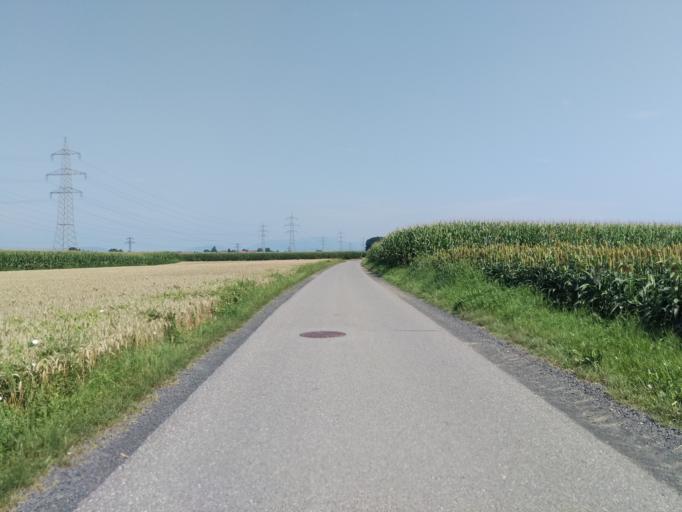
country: AT
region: Styria
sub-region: Politischer Bezirk Graz-Umgebung
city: Werndorf
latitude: 46.9289
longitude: 15.4899
